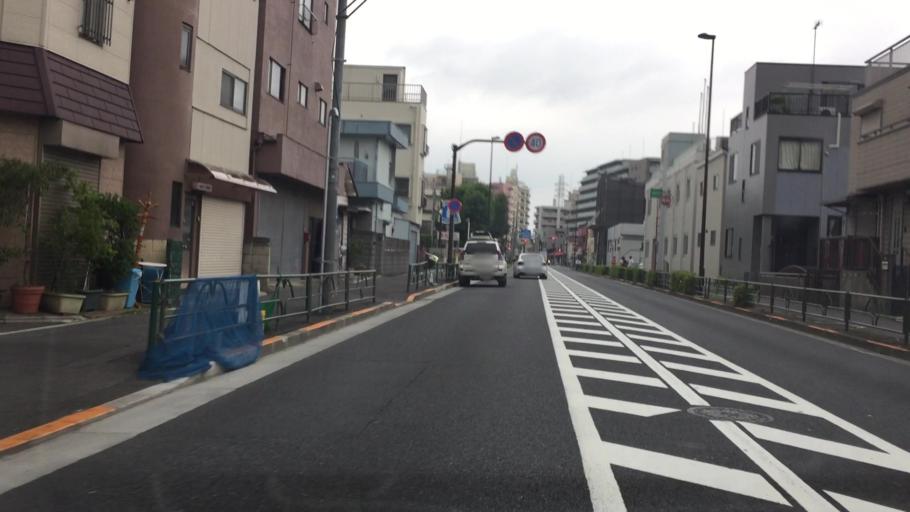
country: JP
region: Saitama
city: Soka
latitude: 35.7535
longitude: 139.7922
